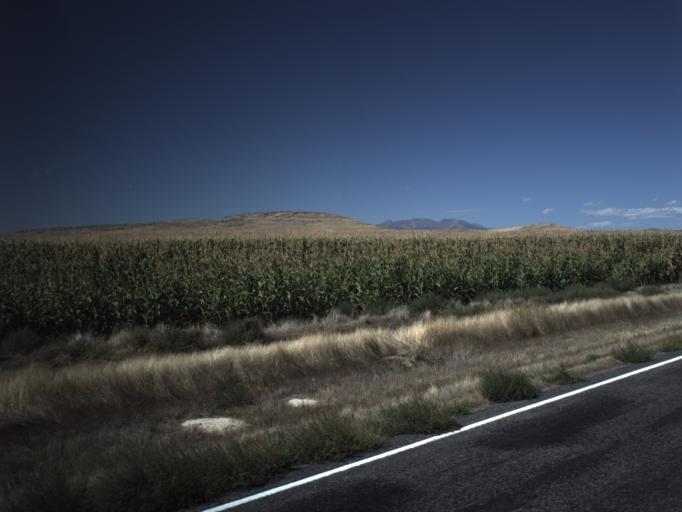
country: US
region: Utah
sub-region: Utah County
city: Genola
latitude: 40.1007
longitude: -111.9590
